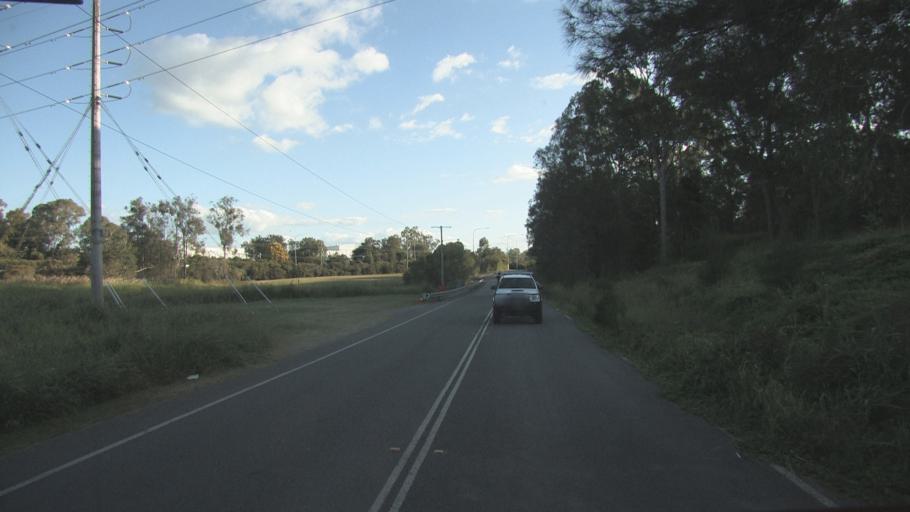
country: AU
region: Queensland
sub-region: Logan
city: Beenleigh
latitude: -27.7112
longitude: 153.1807
